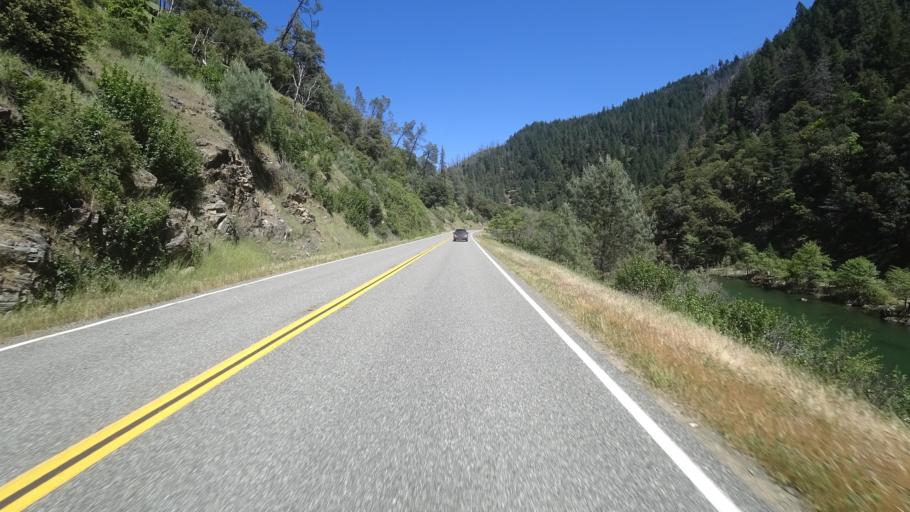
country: US
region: California
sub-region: Trinity County
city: Hayfork
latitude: 40.7565
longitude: -123.1541
